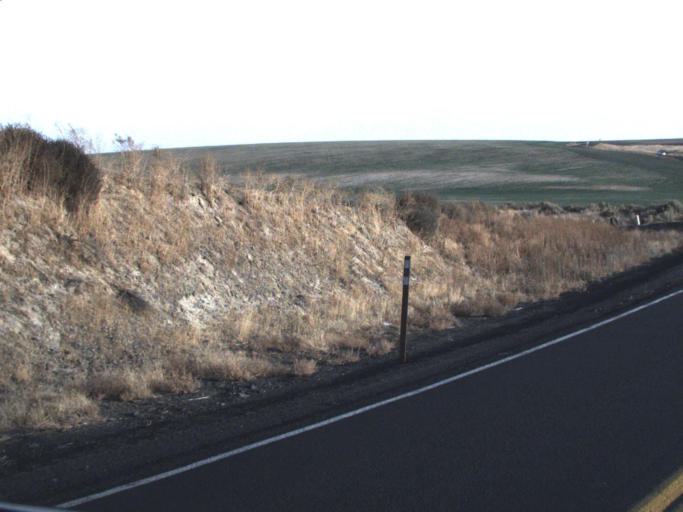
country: US
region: Washington
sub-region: Adams County
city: Ritzville
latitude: 47.1730
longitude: -118.6913
